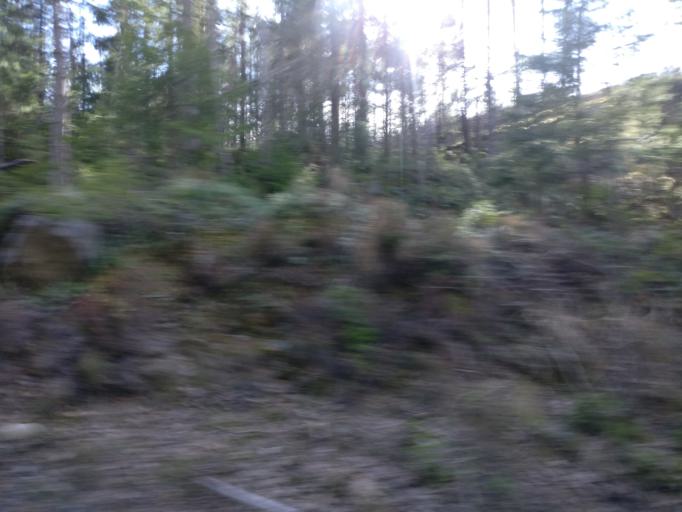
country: FI
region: Varsinais-Suomi
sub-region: Salo
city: Suomusjaervi
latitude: 60.3410
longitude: 23.6486
